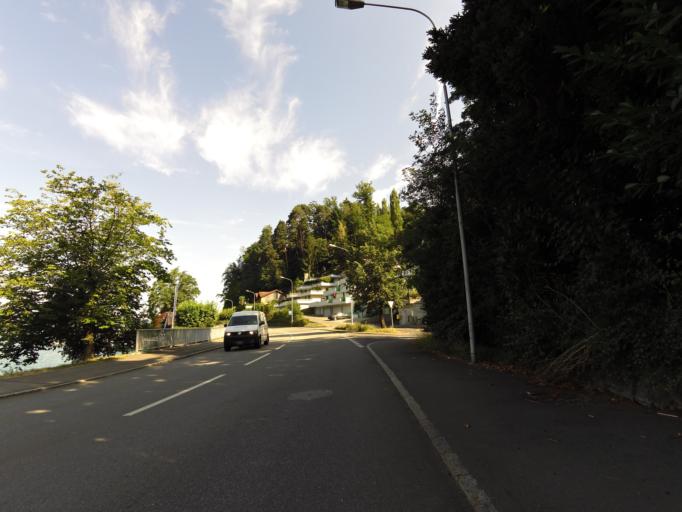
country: CH
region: Zug
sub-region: Zug
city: Walchwil
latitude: 47.0921
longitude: 8.5211
